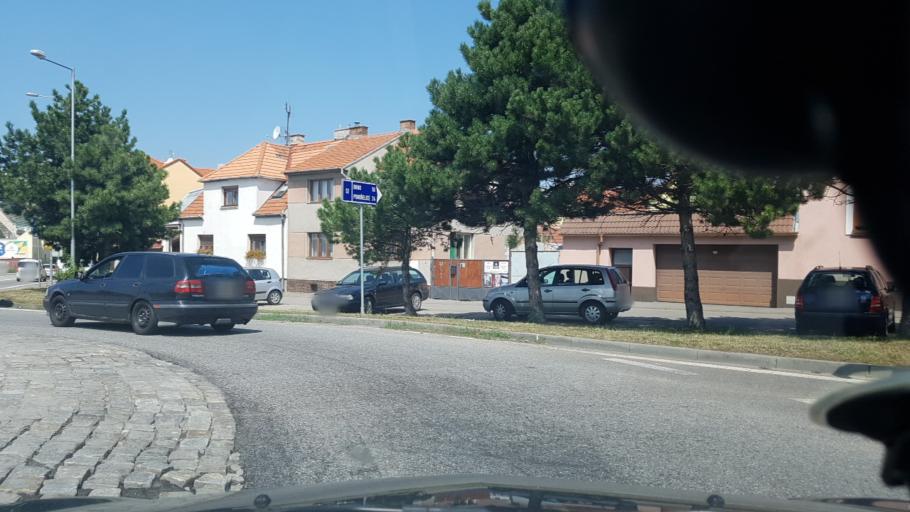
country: CZ
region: South Moravian
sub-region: Okres Breclav
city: Mikulov
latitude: 48.8008
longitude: 16.6306
